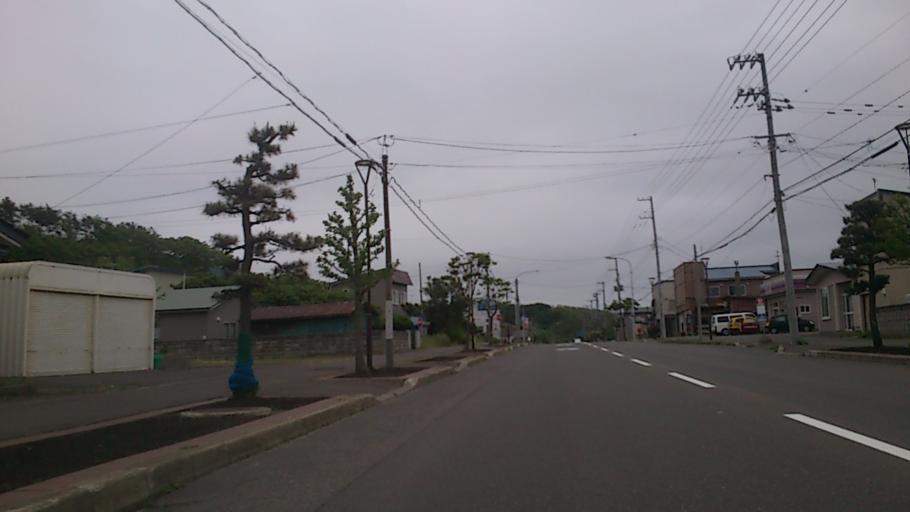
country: JP
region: Hokkaido
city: Iwanai
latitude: 42.4498
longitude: 139.8531
